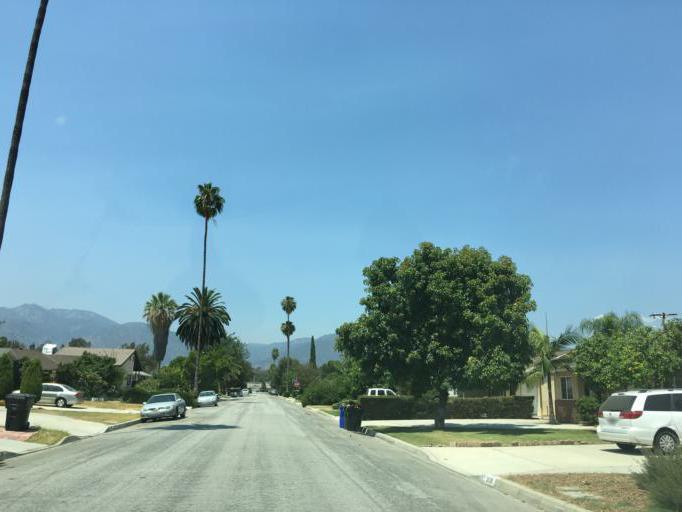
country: US
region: California
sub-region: Los Angeles County
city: Mayflower Village
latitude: 34.1111
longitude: -118.0149
